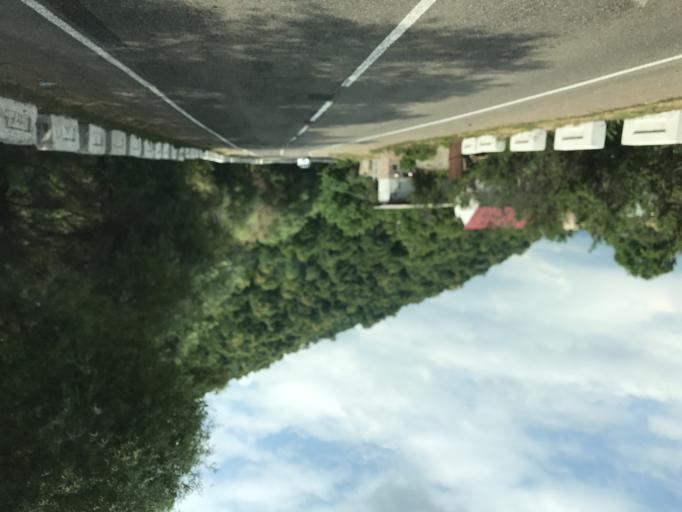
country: AM
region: Tavush
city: Haghartsin
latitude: 40.7733
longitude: 44.9489
